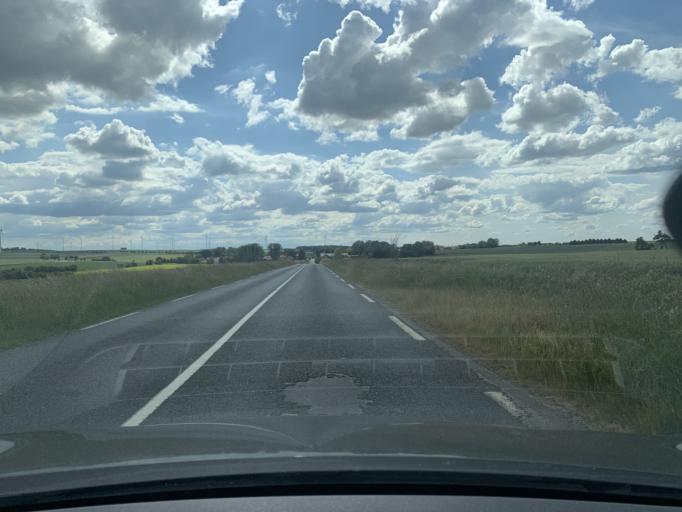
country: FR
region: Nord-Pas-de-Calais
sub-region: Departement du Nord
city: Gouzeaucourt
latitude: 50.0384
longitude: 3.0577
